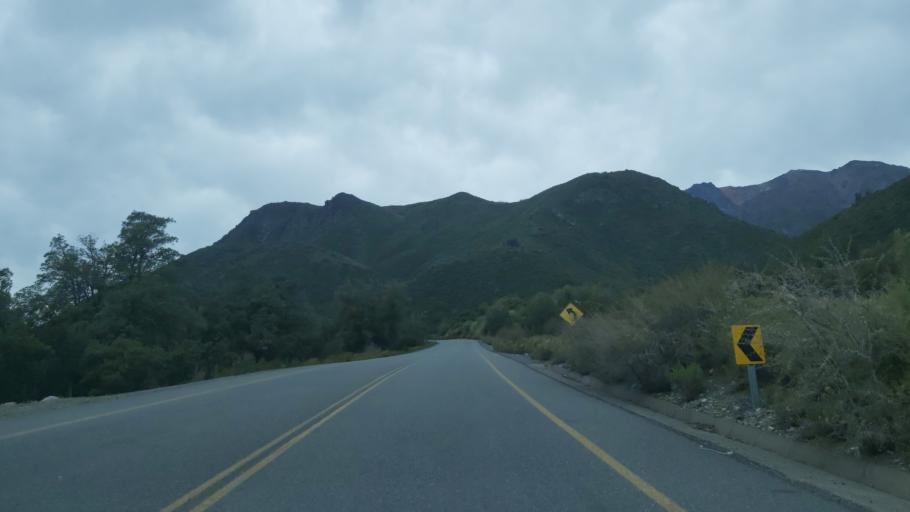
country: CL
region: Maule
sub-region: Provincia de Linares
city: Colbun
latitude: -35.8104
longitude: -70.8759
